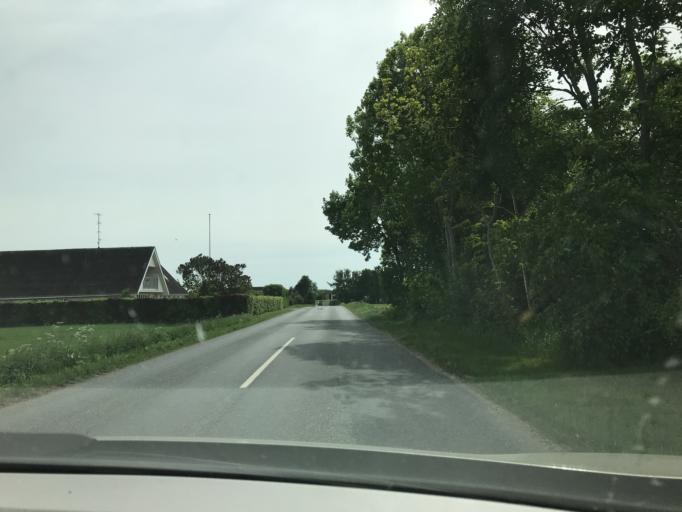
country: DK
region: Central Jutland
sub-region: Norddjurs Kommune
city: Allingabro
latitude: 56.5626
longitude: 10.3059
